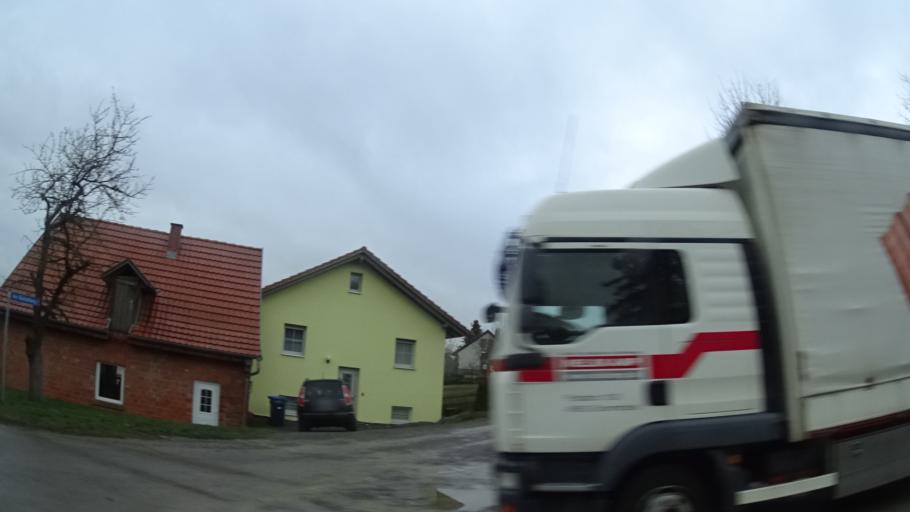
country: DE
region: Thuringia
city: Wolfershausen
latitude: 50.4529
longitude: 10.4563
